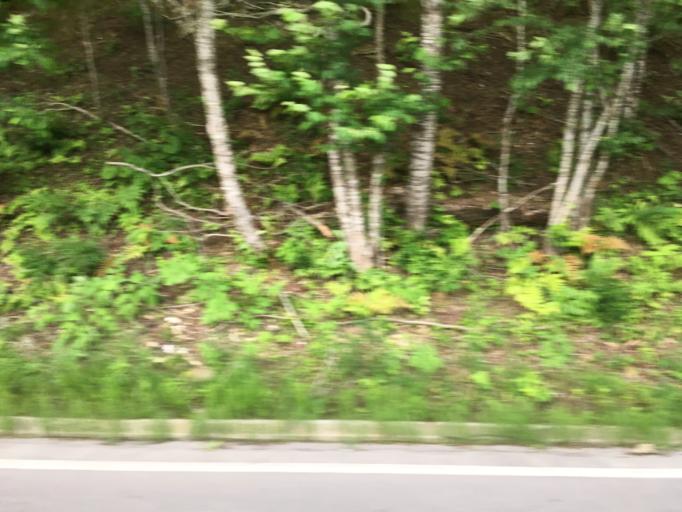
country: JP
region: Fukushima
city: Namie
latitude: 37.4823
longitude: 141.0148
